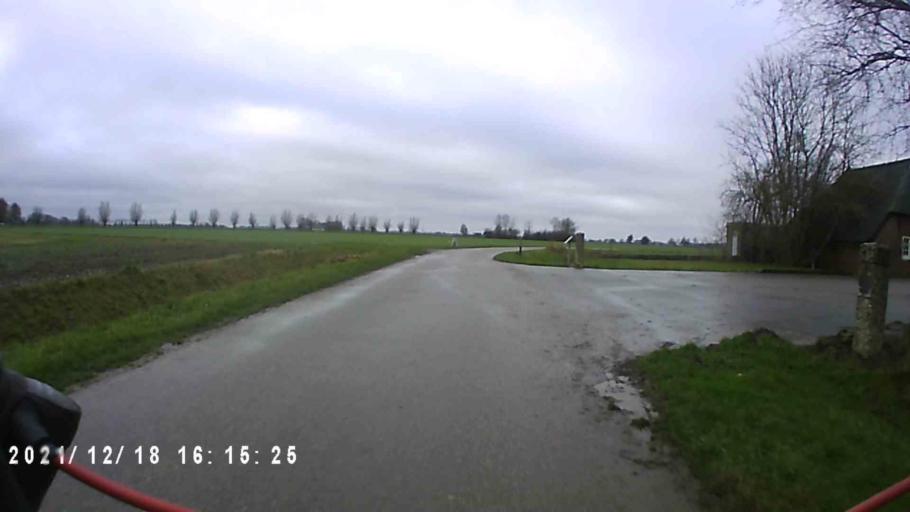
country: NL
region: Friesland
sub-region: Gemeente Dongeradeel
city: Anjum
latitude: 53.3701
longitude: 6.0624
